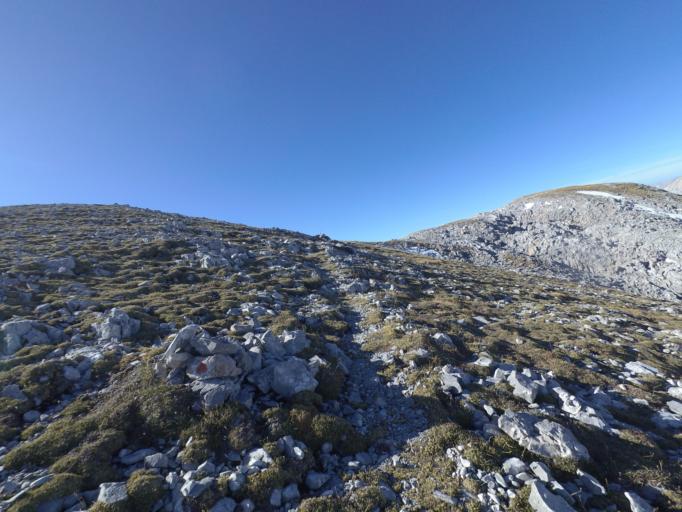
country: AT
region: Salzburg
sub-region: Politischer Bezirk Sankt Johann im Pongau
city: Werfenweng
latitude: 47.5010
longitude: 13.2273
